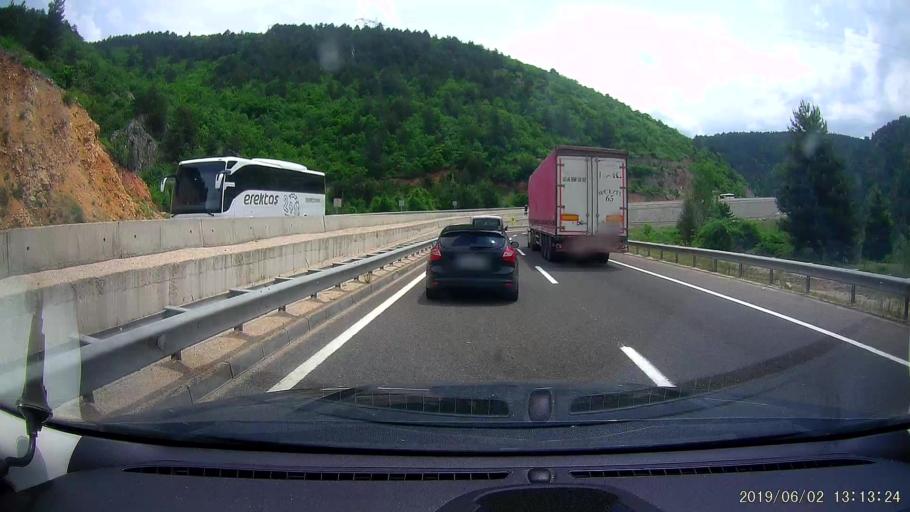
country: TR
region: Karabuk
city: Gozyeri
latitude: 40.8520
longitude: 32.6431
